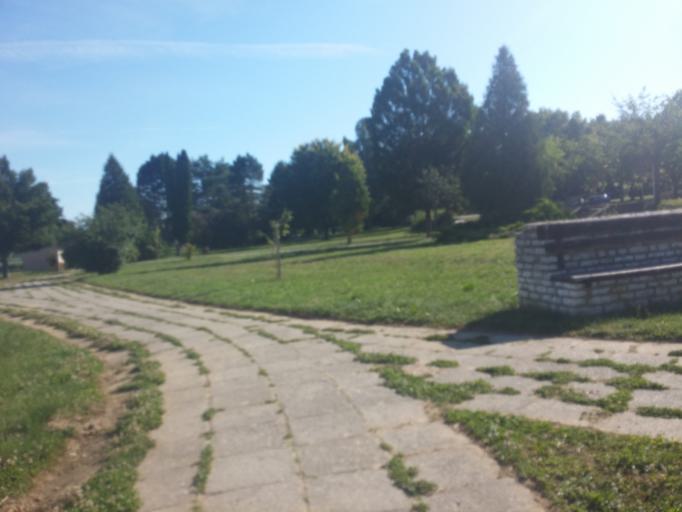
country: HU
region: Zala
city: Nagykanizsa
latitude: 46.4448
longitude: 17.0353
